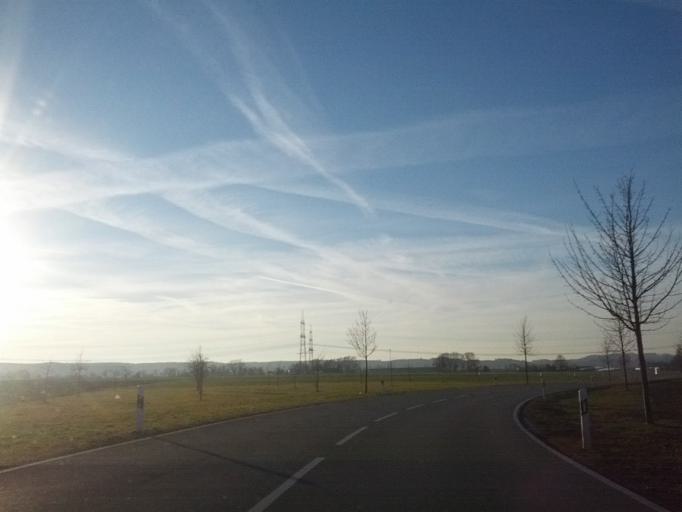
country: DE
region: Bavaria
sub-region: Swabia
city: Wolfertschwenden
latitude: 47.8880
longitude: 10.2666
